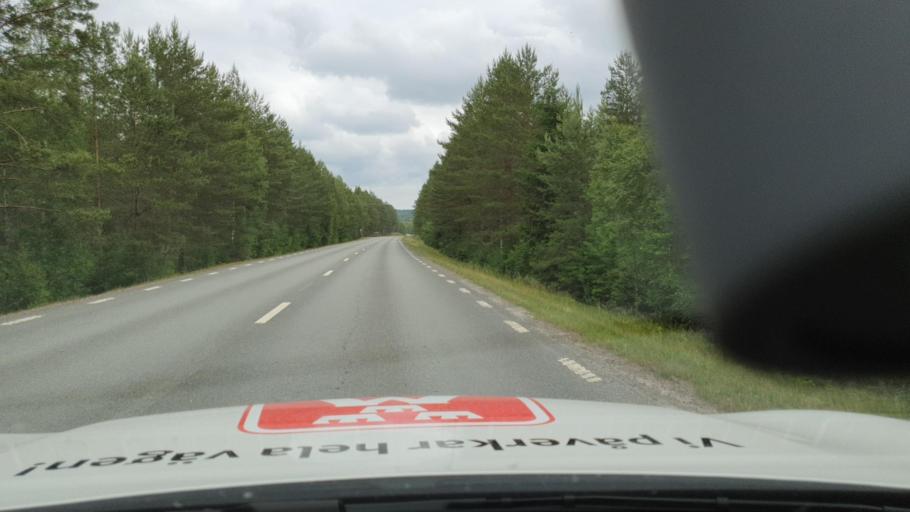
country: SE
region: Vaestra Goetaland
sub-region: Tidaholms Kommun
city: Olofstorp
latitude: 58.2155
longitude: 14.0841
